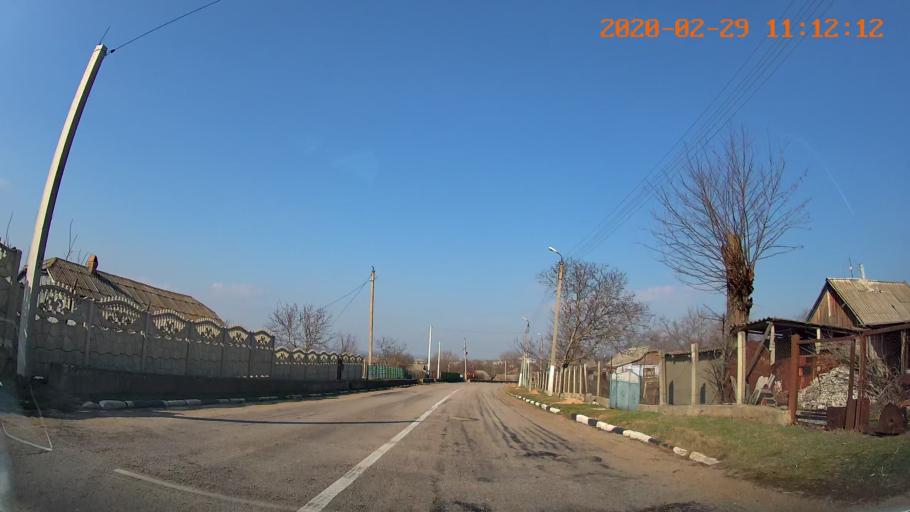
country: MD
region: Telenesti
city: Dubasari
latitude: 47.2606
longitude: 29.1877
